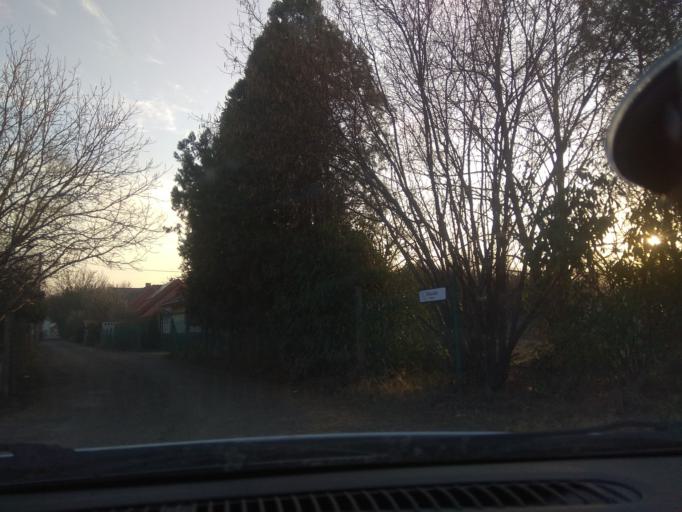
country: HU
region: Pest
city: Szigetszentmiklos
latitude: 47.3352
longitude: 19.0293
